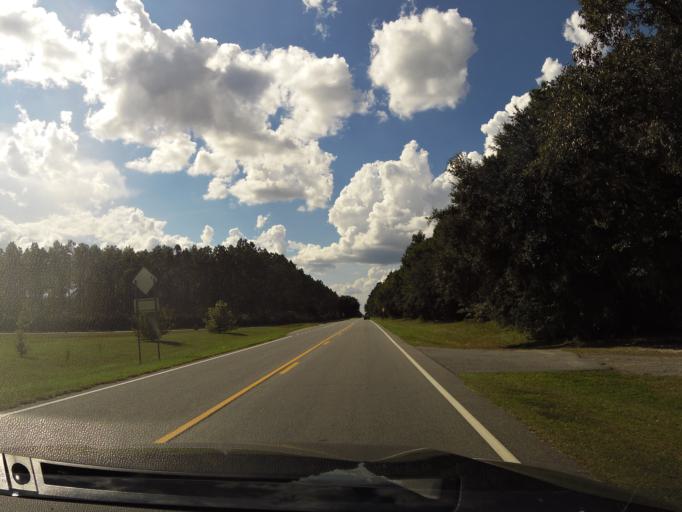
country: US
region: Georgia
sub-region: Lowndes County
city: Valdosta
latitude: 30.8068
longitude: -83.2116
